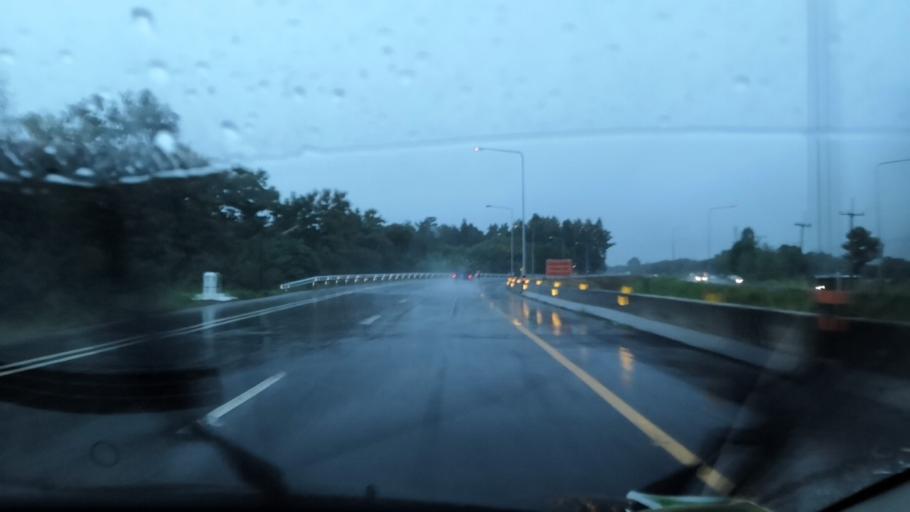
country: TH
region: Chiang Mai
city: San Pa Tong
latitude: 18.6666
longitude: 98.8772
